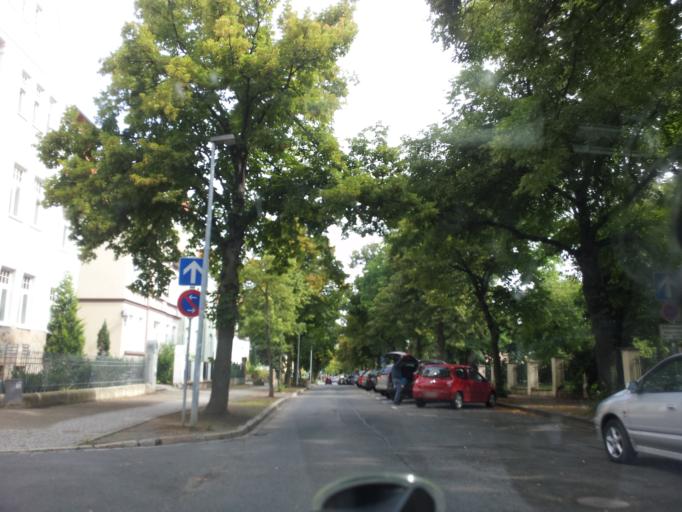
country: DE
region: Saxony-Anhalt
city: Quedlinburg
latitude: 51.7899
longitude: 11.1381
